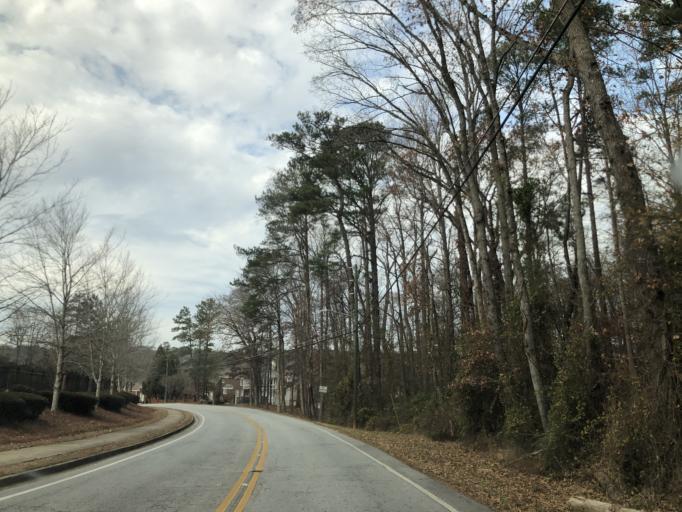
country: US
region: Georgia
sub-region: DeKalb County
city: Panthersville
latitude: 33.6647
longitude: -84.2047
